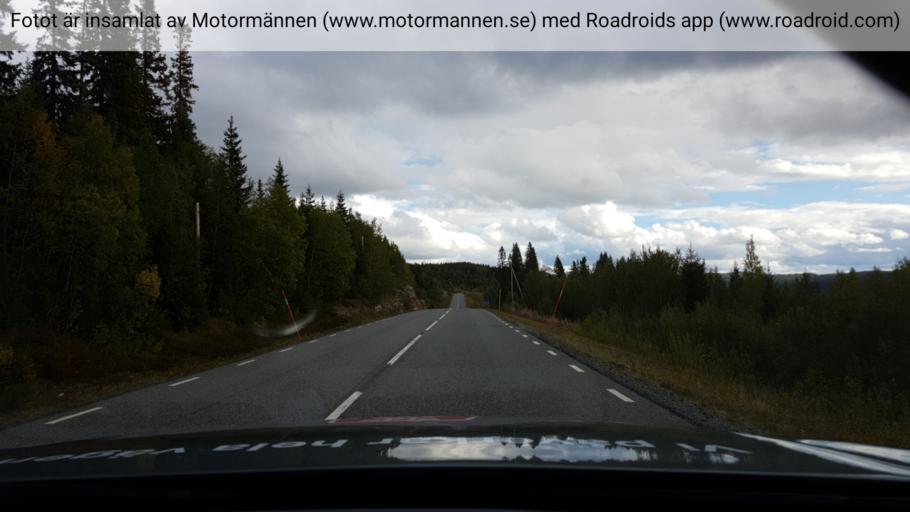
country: SE
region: Jaemtland
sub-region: Are Kommun
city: Are
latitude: 63.6398
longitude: 13.0882
